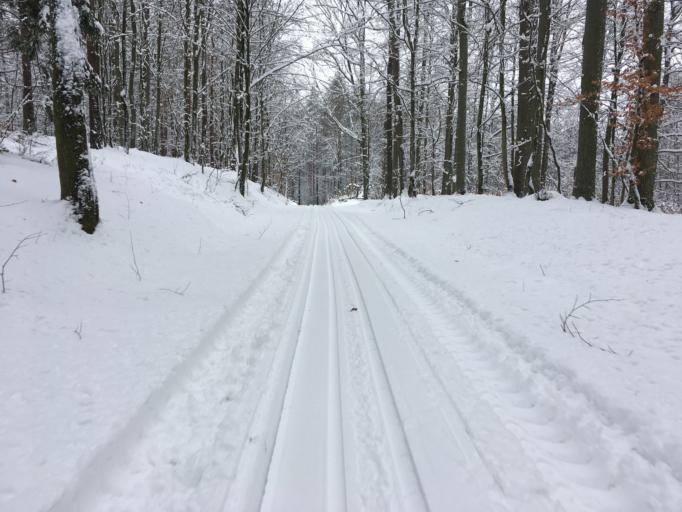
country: PL
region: Kujawsko-Pomorskie
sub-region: Powiat brodnicki
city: Gorzno
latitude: 53.1892
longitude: 19.6869
